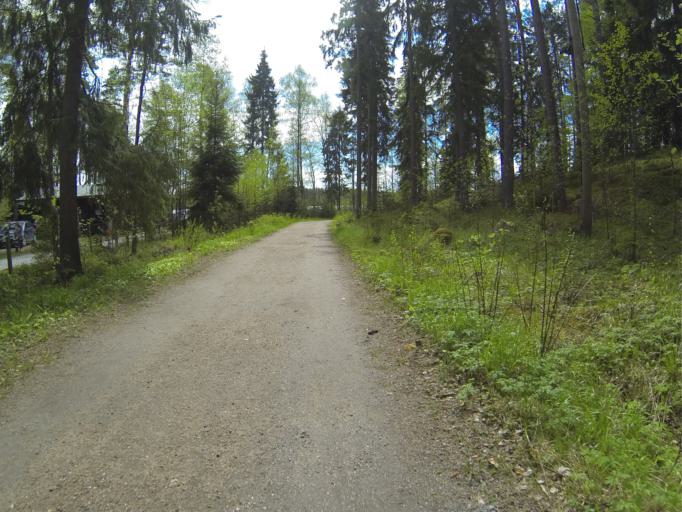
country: FI
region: Varsinais-Suomi
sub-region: Salo
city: Halikko
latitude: 60.3009
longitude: 23.0769
